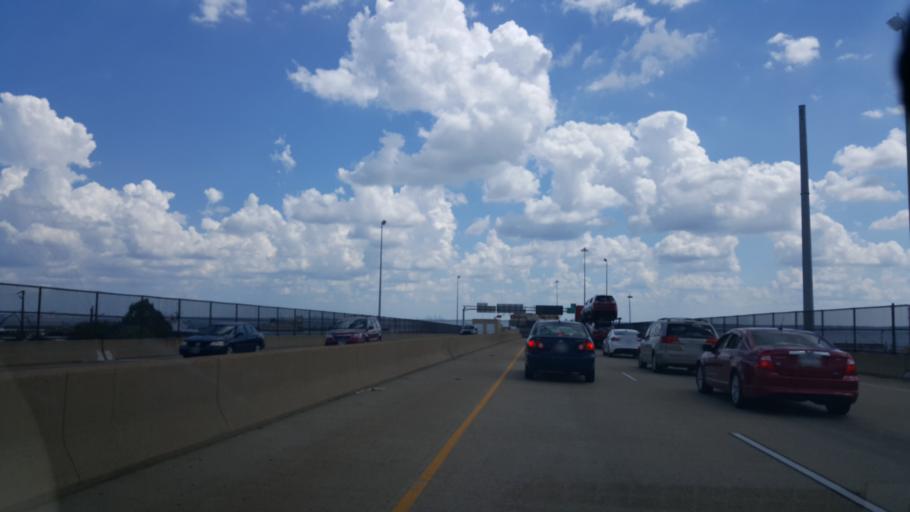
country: US
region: Virginia
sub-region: City of Newport News
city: Newport News
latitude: 36.9639
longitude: -76.4129
